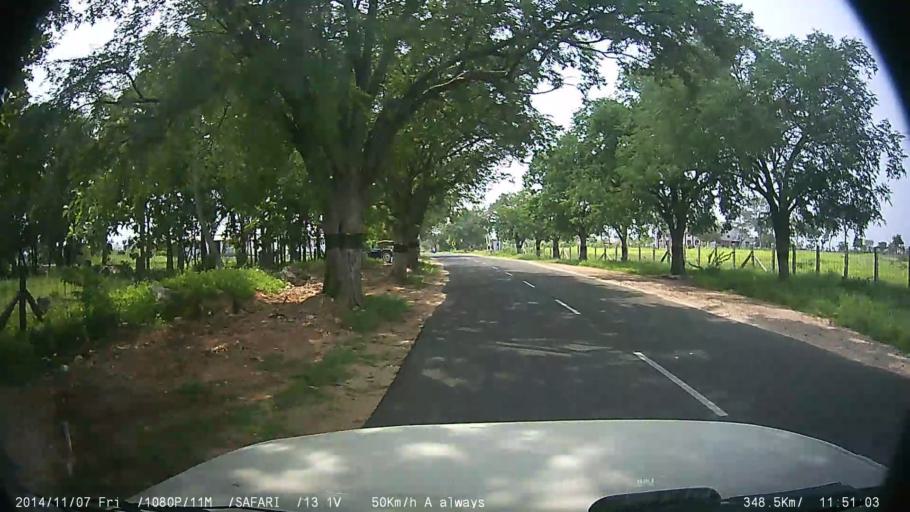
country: IN
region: Tamil Nadu
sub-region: Tiruppur
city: Avinashi
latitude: 11.1484
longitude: 77.2645
